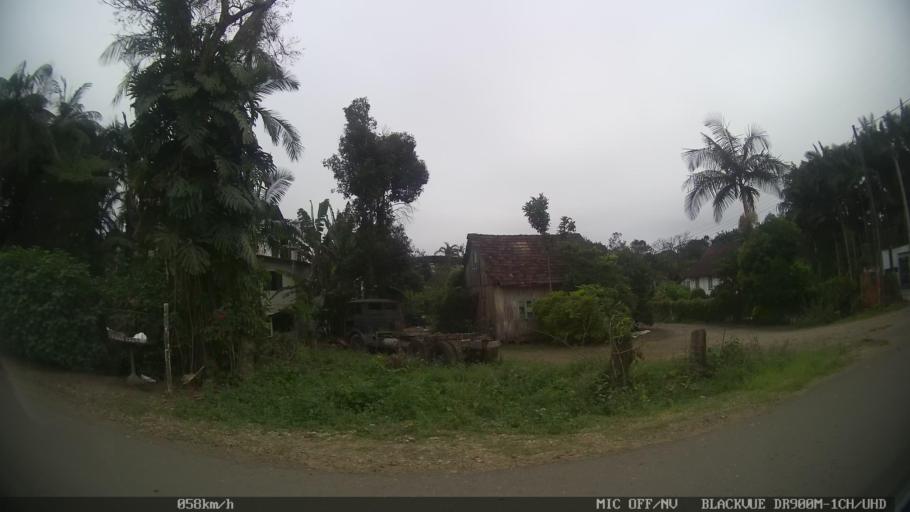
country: BR
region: Santa Catarina
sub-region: Joinville
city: Joinville
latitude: -26.1966
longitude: -48.9225
